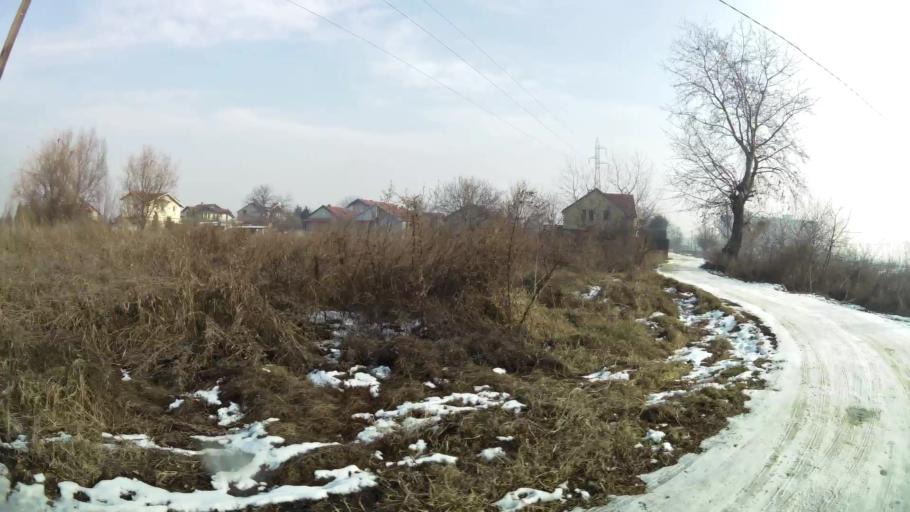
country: MK
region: Kisela Voda
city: Kisela Voda
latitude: 41.9951
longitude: 21.5171
